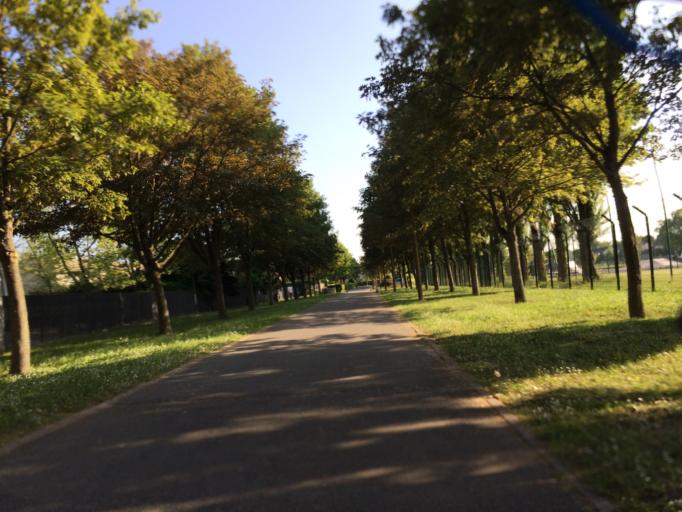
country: FR
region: Ile-de-France
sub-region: Departement de l'Essonne
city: Bondoufle
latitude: 48.6167
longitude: 2.3883
